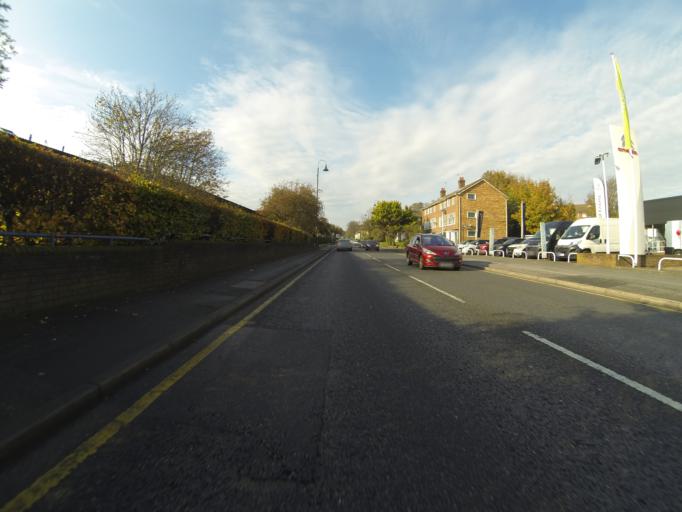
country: GB
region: England
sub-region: Greater London
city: Bexley
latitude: 51.4514
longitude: 0.1767
